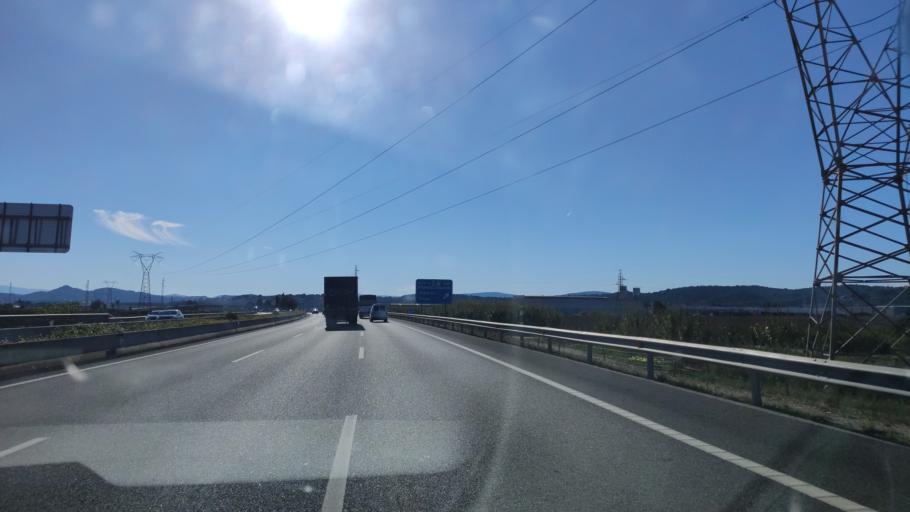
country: ES
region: Valencia
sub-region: Provincia de Valencia
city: Alberic
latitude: 39.1266
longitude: -0.5295
